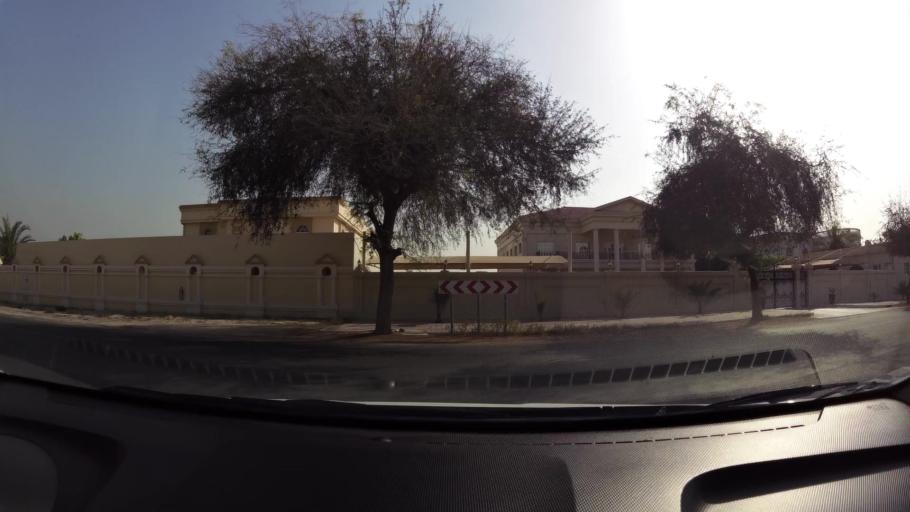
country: AE
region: Ash Shariqah
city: Sharjah
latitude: 25.3080
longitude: 55.3444
